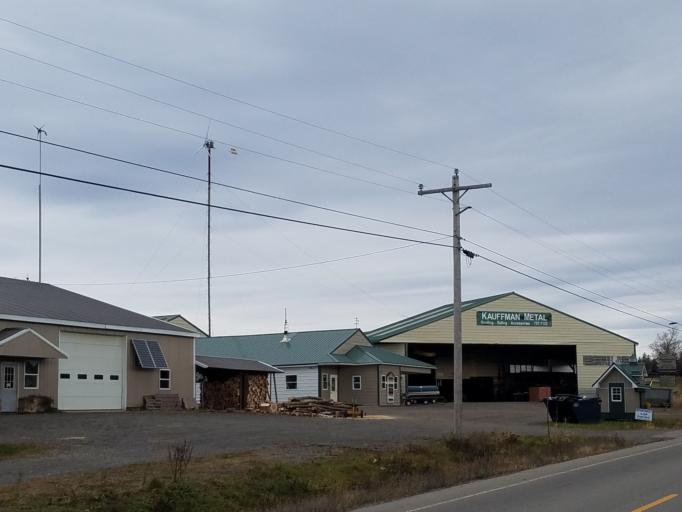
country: US
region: Maine
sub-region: Aroostook County
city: Hodgdon
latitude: 46.1434
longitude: -68.0869
